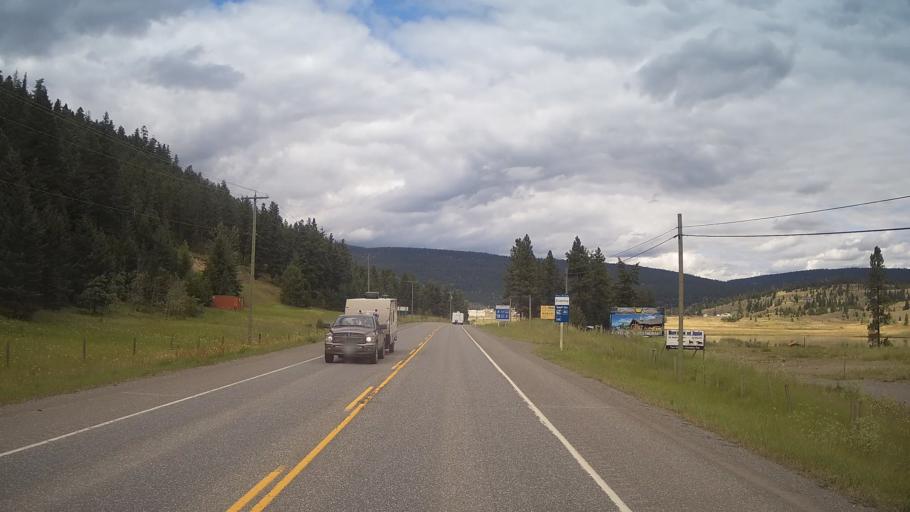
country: CA
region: British Columbia
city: Cache Creek
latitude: 51.0686
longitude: -121.5822
